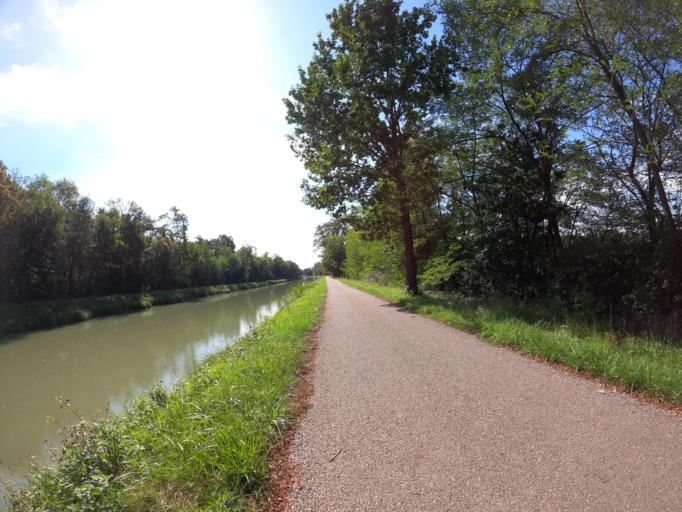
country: FR
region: Midi-Pyrenees
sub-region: Departement du Tarn-et-Garonne
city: Montech
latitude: 43.9425
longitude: 1.2534
